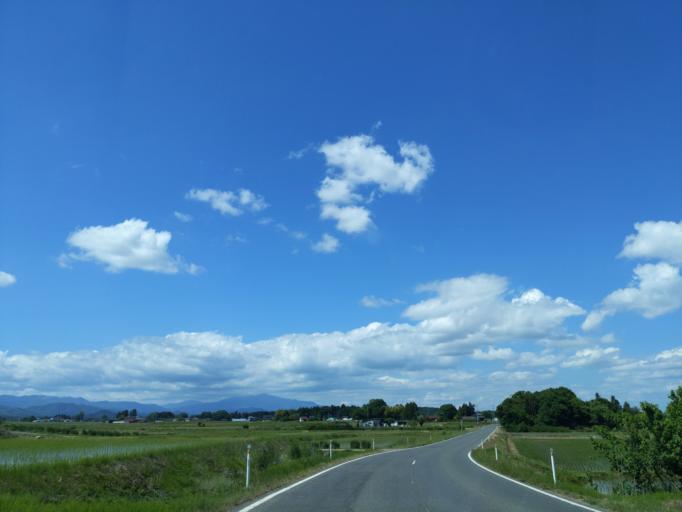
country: JP
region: Fukushima
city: Koriyama
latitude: 37.3760
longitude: 140.2940
